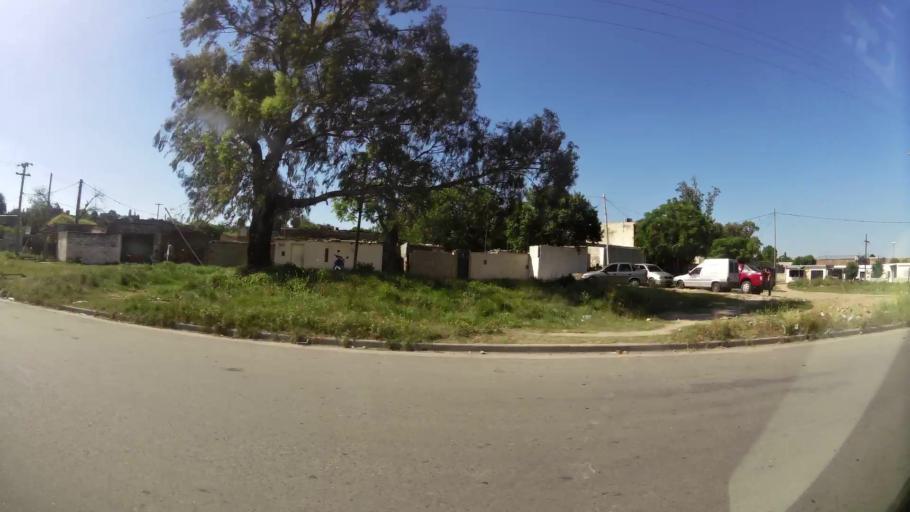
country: AR
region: Cordoba
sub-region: Departamento de Capital
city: Cordoba
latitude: -31.4180
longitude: -64.1491
